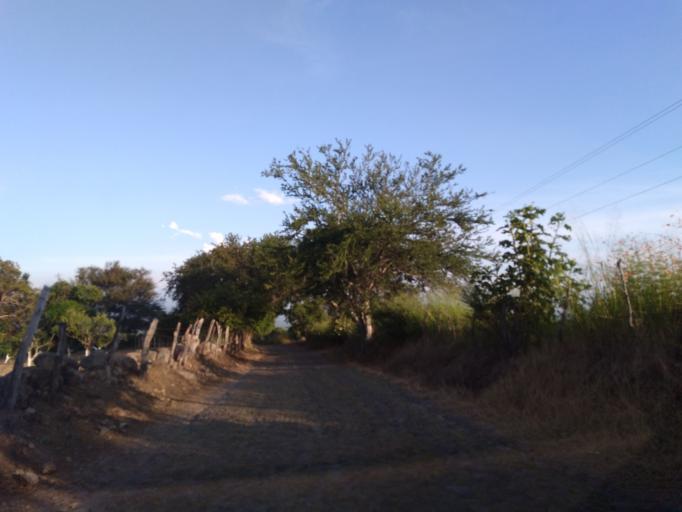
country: MX
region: Jalisco
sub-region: Tonila
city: San Marcos
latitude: 19.4605
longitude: -103.5238
